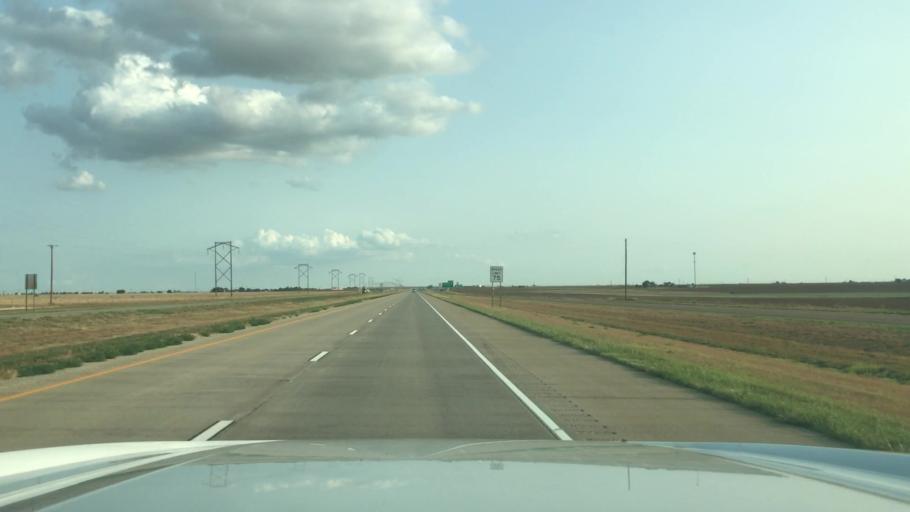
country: US
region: Texas
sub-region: Swisher County
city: Tulia
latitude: 34.5556
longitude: -101.7950
